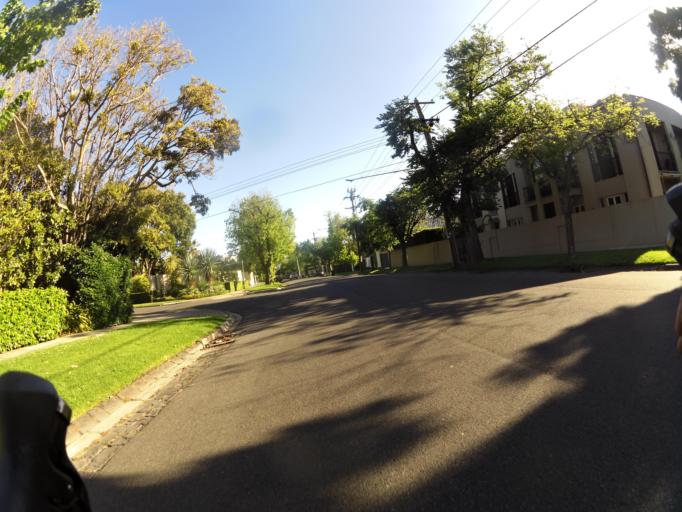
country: AU
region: Victoria
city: Toorak
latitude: -37.8474
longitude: 145.0190
